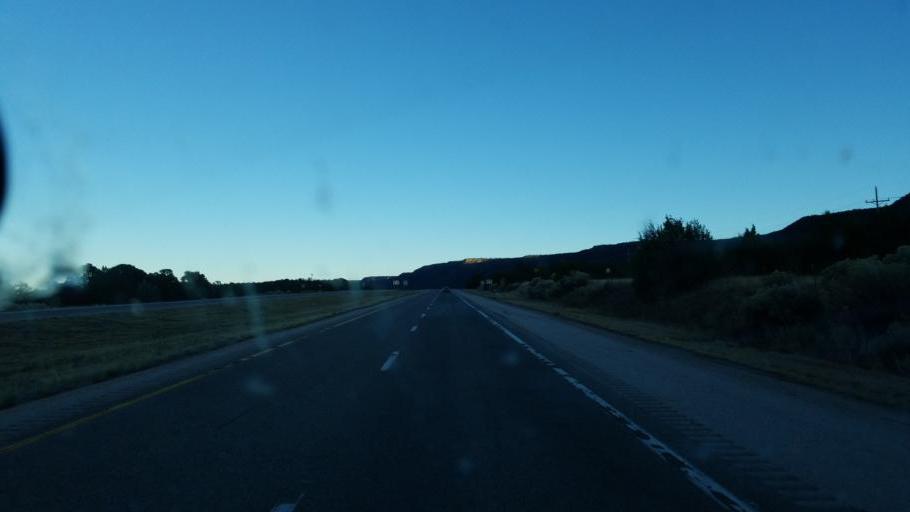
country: US
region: New Mexico
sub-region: San Miguel County
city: Pecos
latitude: 35.4402
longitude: -105.6120
